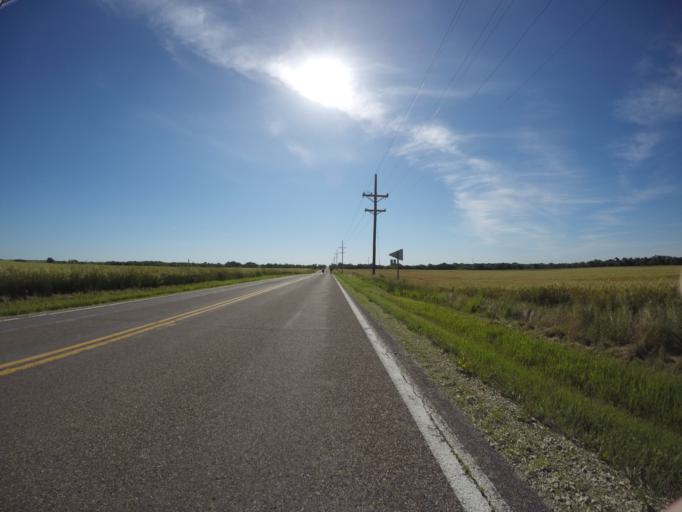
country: US
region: Kansas
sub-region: Mitchell County
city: Beloit
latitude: 39.6393
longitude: -97.9528
